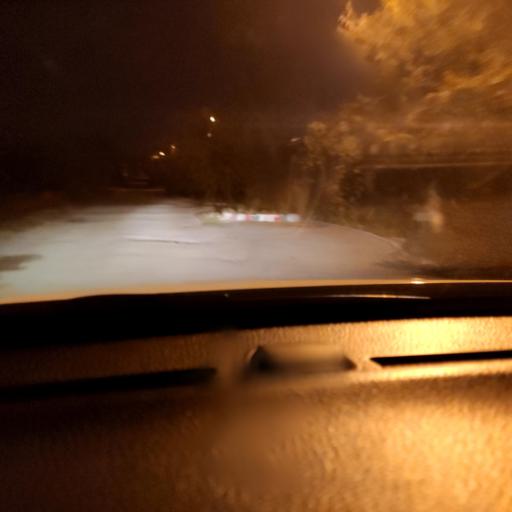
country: RU
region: Voronezj
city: Voronezh
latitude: 51.6599
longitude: 39.2720
